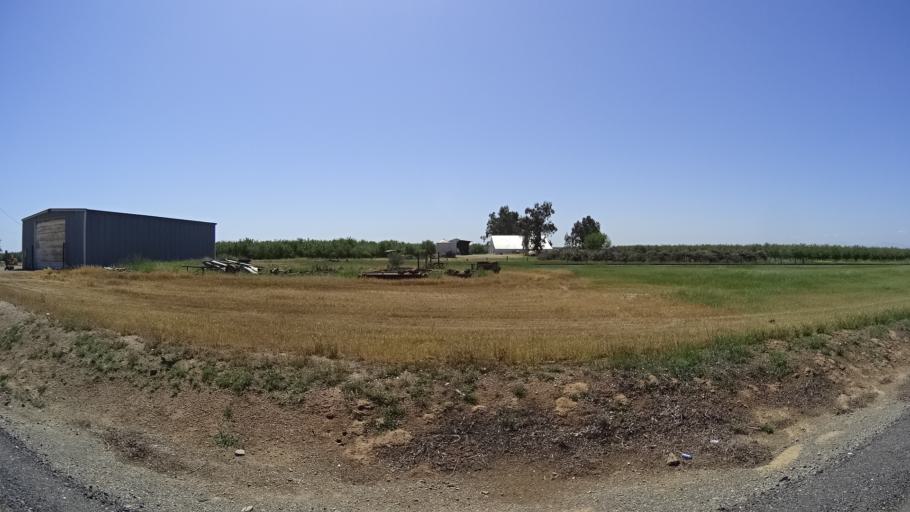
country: US
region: California
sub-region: Glenn County
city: Hamilton City
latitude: 39.7667
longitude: -122.0919
